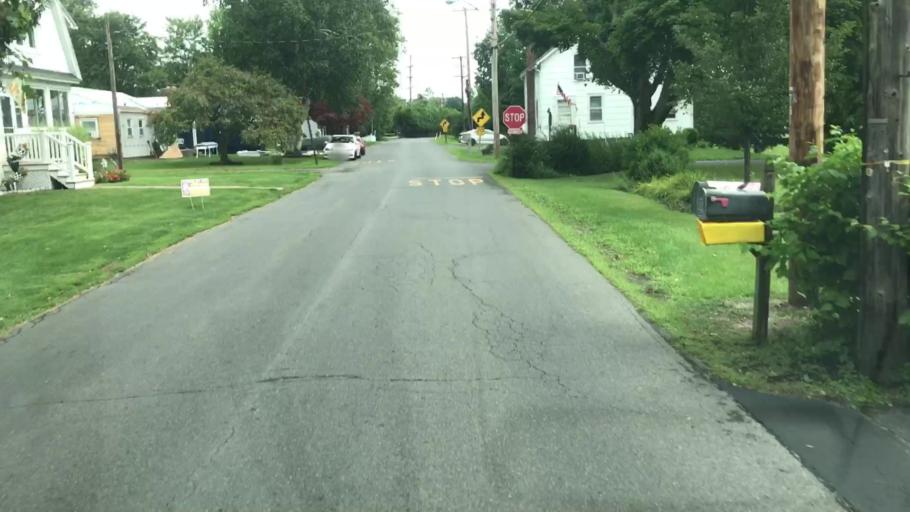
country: US
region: New York
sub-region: Cayuga County
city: Melrose Park
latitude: 42.9125
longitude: -76.5373
